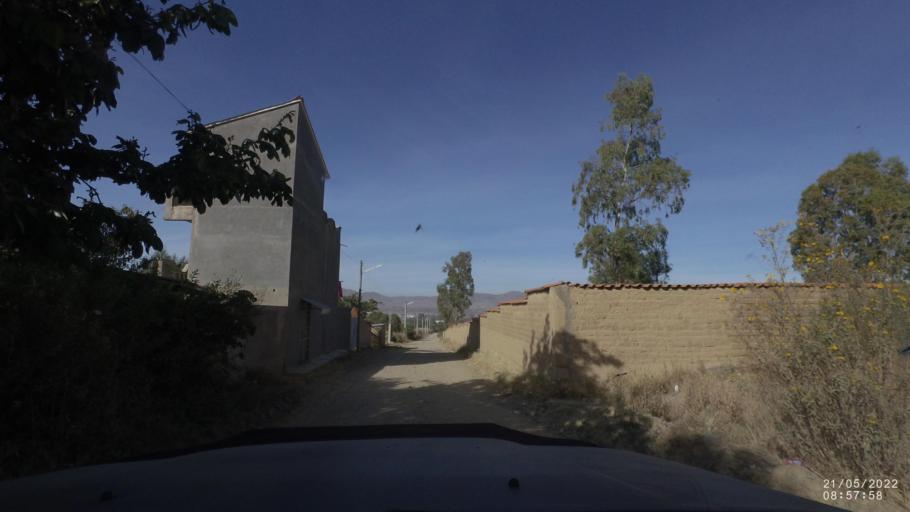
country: BO
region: Cochabamba
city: Cochabamba
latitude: -17.3790
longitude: -66.0384
